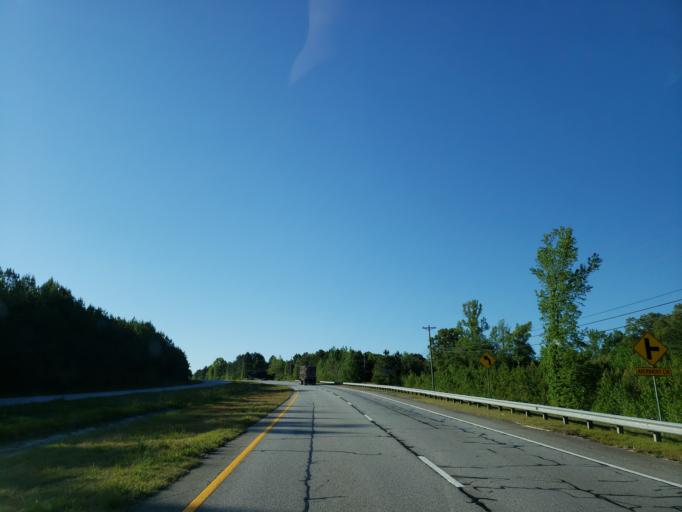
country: US
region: Georgia
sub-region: Haralson County
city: Buchanan
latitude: 33.8669
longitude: -85.2144
